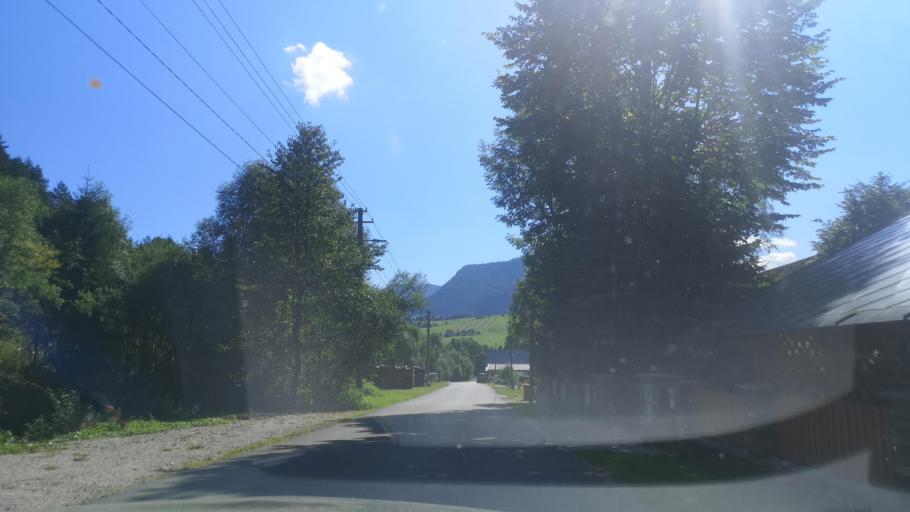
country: SK
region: Zilinsky
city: Oravska Lesna
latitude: 49.2841
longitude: 19.1350
